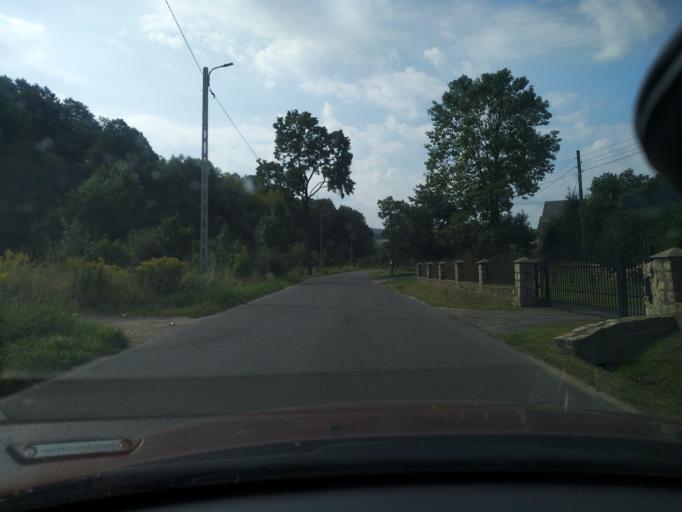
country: PL
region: Lower Silesian Voivodeship
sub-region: Powiat jeleniogorski
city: Stara Kamienica
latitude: 50.9073
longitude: 15.5692
